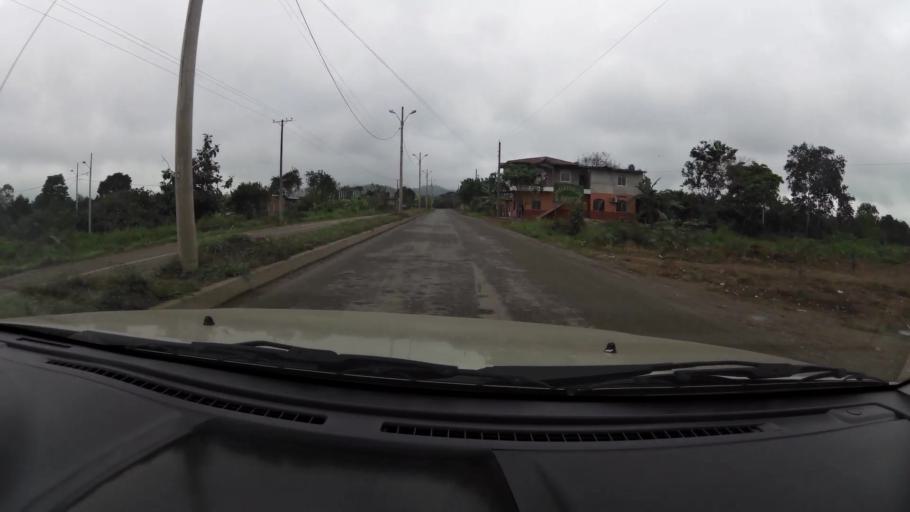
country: EC
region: El Oro
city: Pasaje
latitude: -3.3423
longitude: -79.8028
